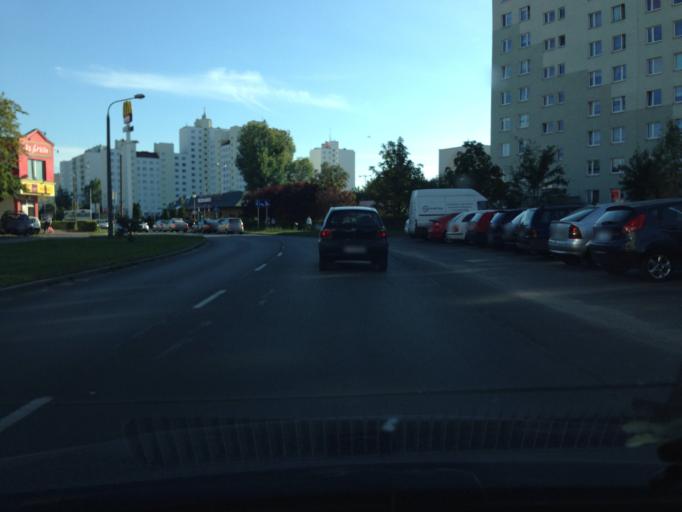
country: PL
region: Kujawsko-Pomorskie
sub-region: Powiat torunski
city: Lubicz Dolny
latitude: 53.0273
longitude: 18.6738
